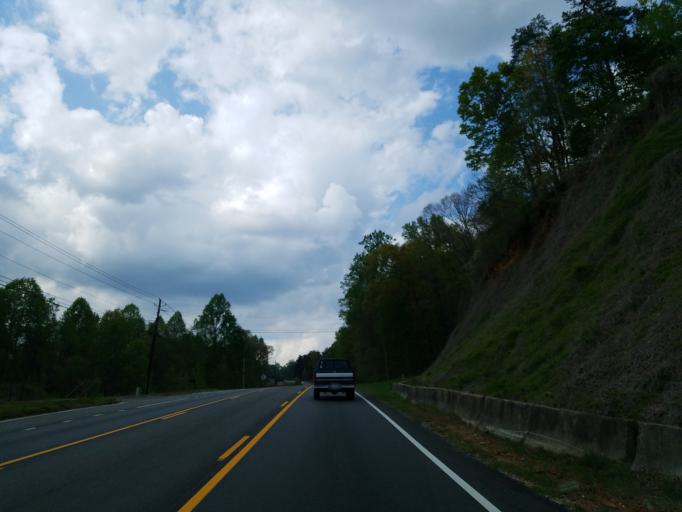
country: US
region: Georgia
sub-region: Lumpkin County
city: Dahlonega
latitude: 34.5134
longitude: -83.9755
